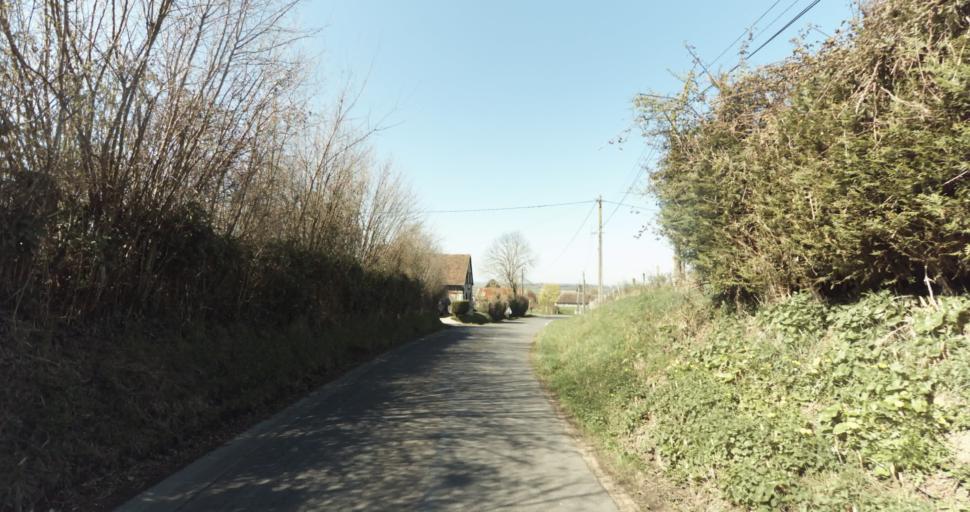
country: FR
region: Lower Normandy
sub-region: Departement du Calvados
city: Saint-Pierre-sur-Dives
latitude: 49.0178
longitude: 0.0477
